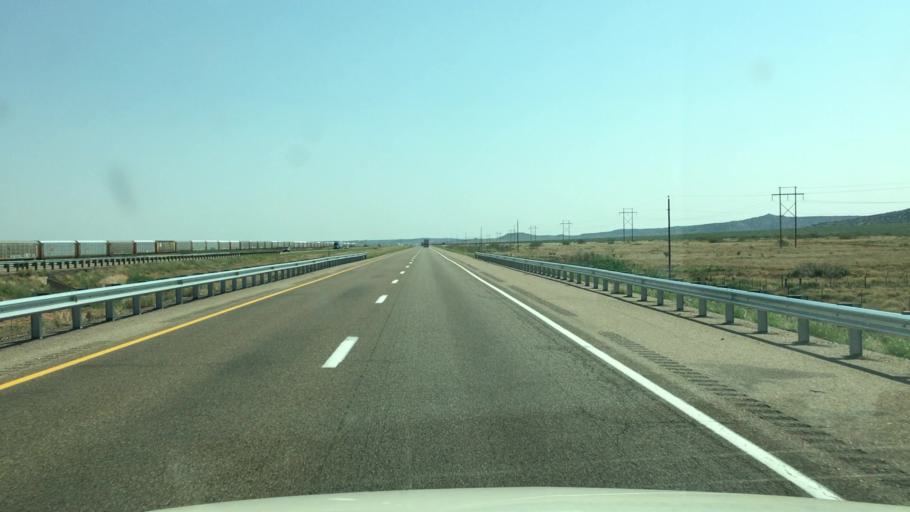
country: US
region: New Mexico
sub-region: Quay County
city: Tucumcari
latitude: 35.1068
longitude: -104.0218
